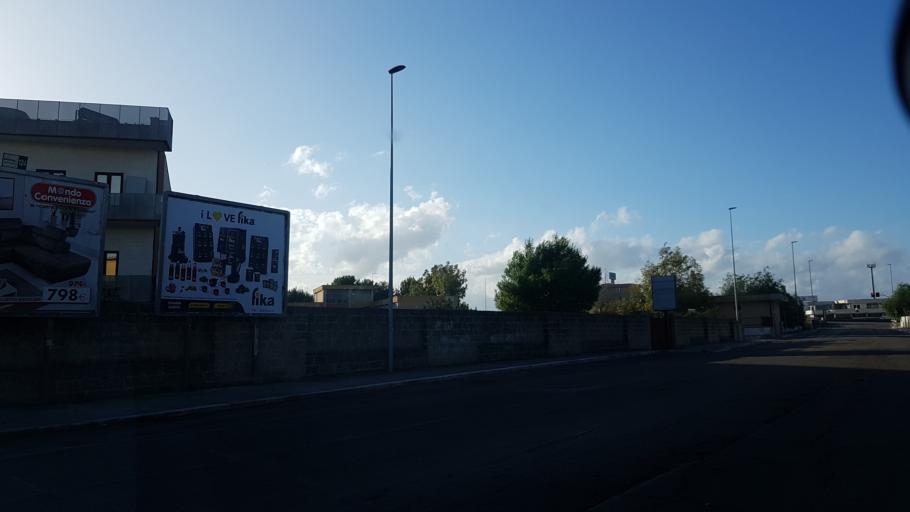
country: IT
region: Apulia
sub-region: Provincia di Lecce
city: Lecce
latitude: 40.3537
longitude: 18.1538
